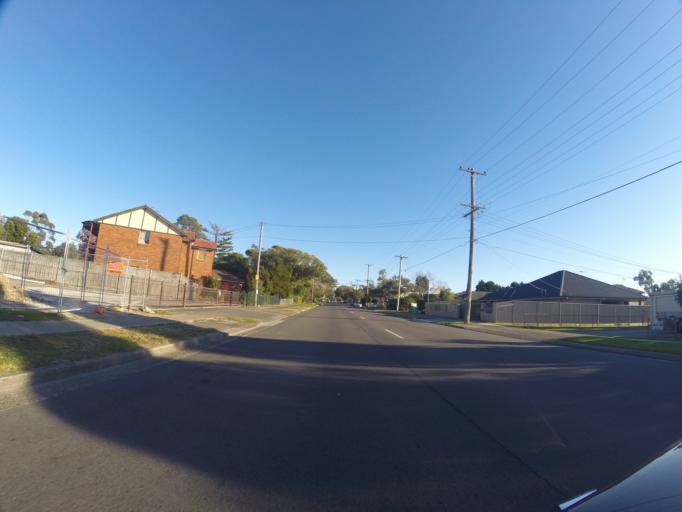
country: AU
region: New South Wales
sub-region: Sutherland Shire
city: Gymea Bay
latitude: -34.0484
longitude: 151.0863
